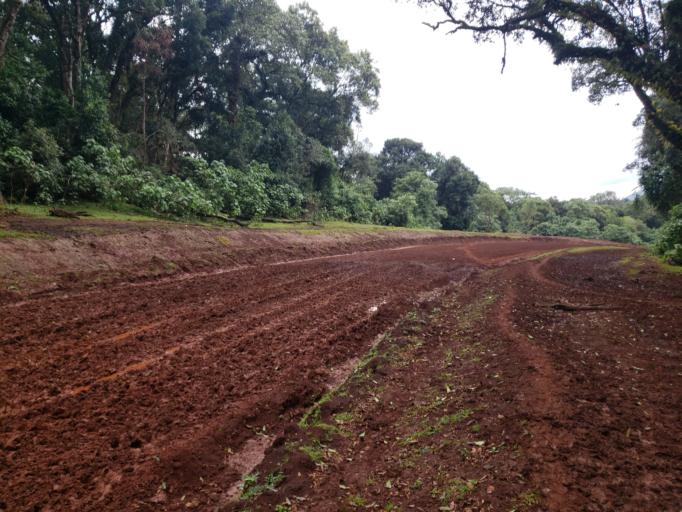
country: ET
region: Oromiya
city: Dodola
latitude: 6.6150
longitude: 39.4204
